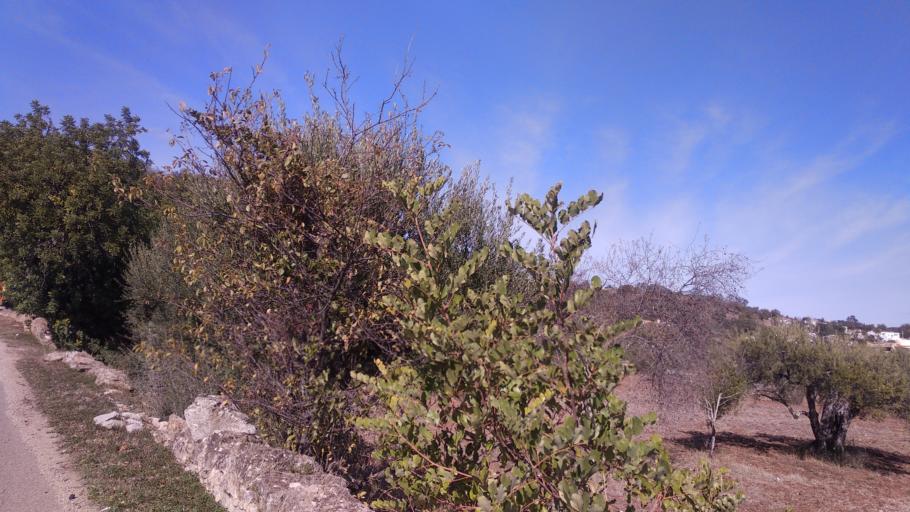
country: PT
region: Faro
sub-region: Sao Bras de Alportel
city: Sao Bras de Alportel
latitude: 37.1593
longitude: -7.8956
